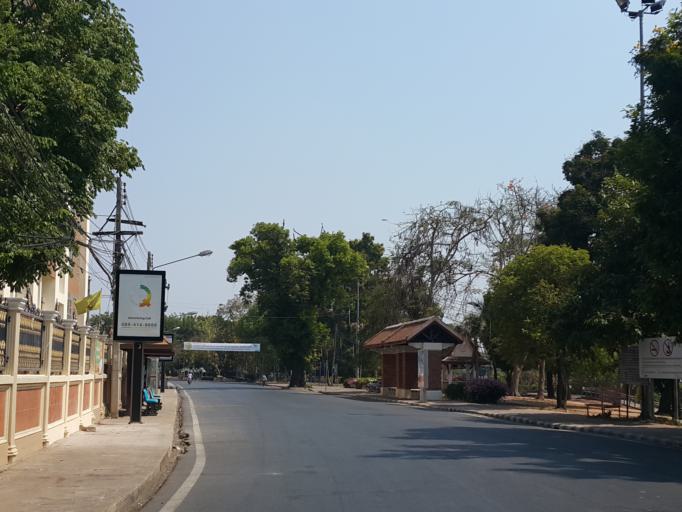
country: TH
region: Phitsanulok
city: Phitsanulok
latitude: 16.8198
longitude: 100.2594
